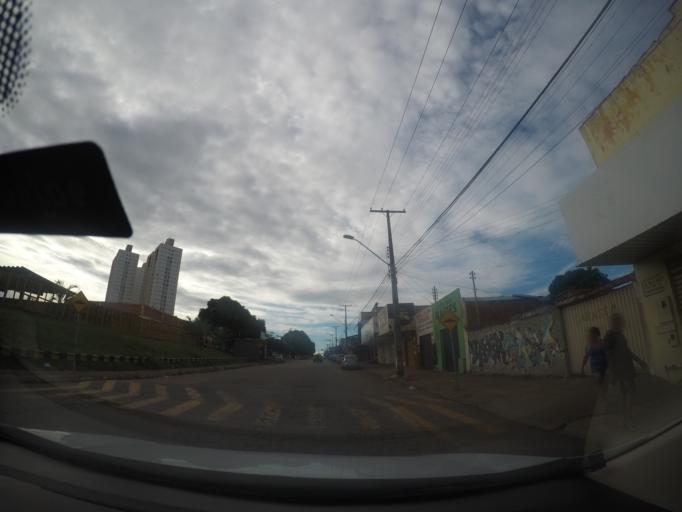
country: BR
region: Goias
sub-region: Goiania
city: Goiania
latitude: -16.6590
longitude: -49.3265
